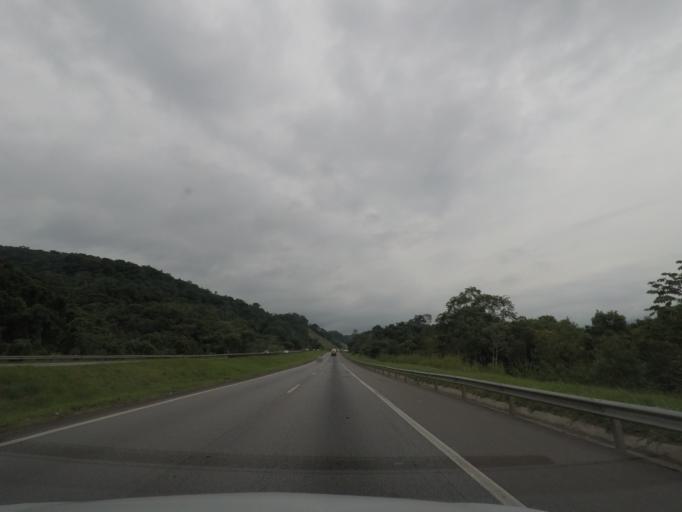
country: BR
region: Sao Paulo
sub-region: Miracatu
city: Miracatu
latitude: -24.1784
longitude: -47.3492
